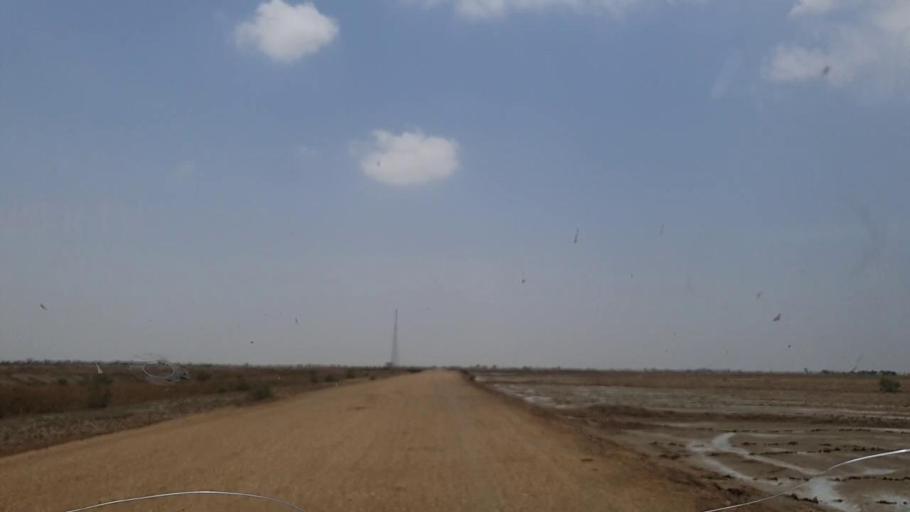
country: PK
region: Sindh
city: Johi
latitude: 26.7812
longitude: 67.6498
